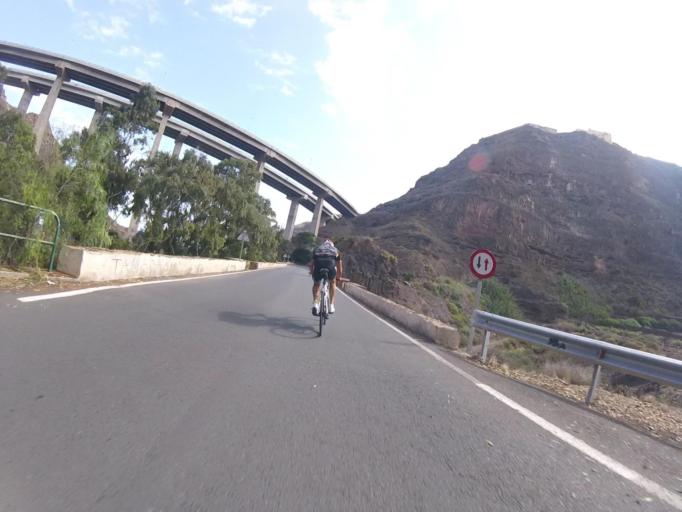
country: ES
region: Canary Islands
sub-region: Provincia de Las Palmas
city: Moya
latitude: 28.1377
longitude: -15.5917
